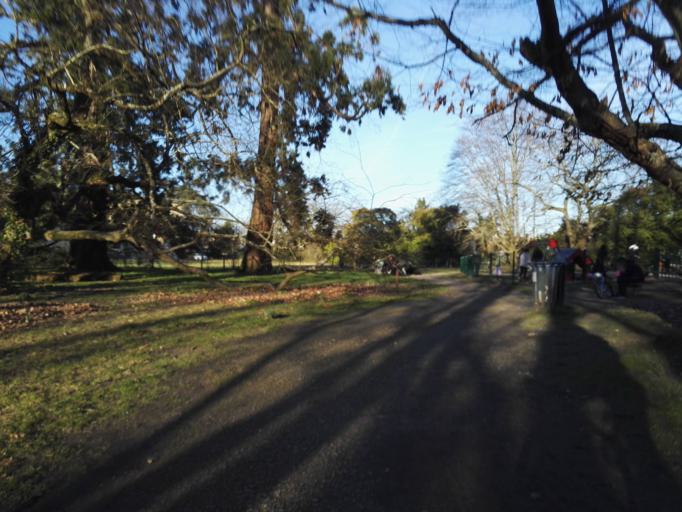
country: FR
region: Aquitaine
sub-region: Departement de la Gironde
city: Merignac
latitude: 44.8208
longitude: -0.6167
